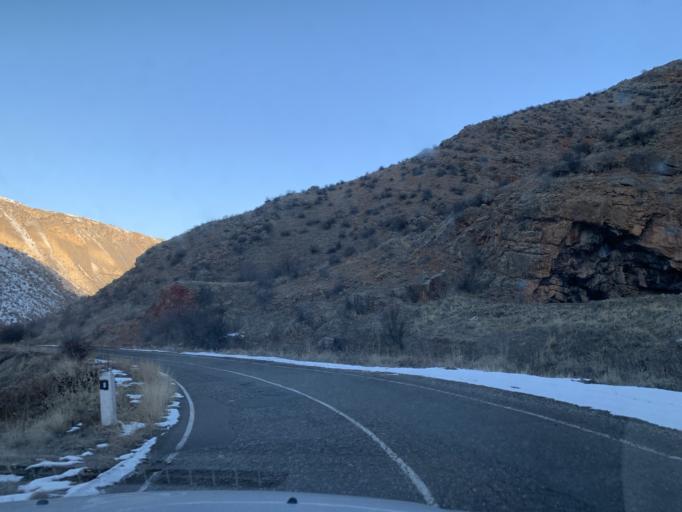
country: AM
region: Vayots' Dzori Marz
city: Areni
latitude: 39.6906
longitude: 45.2202
